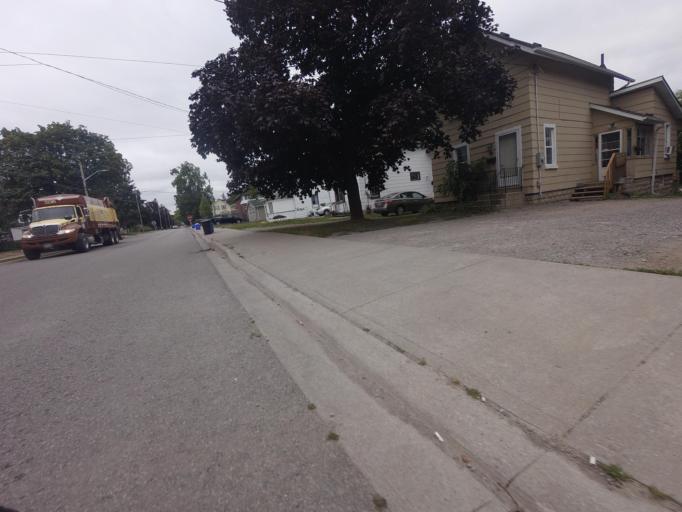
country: CA
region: Ontario
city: Omemee
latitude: 44.3468
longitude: -78.7454
